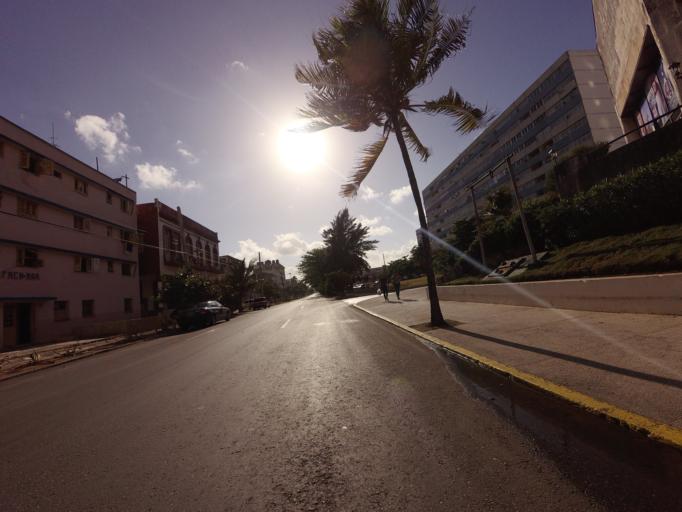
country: CU
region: La Habana
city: Havana
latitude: 23.1388
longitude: -82.4030
